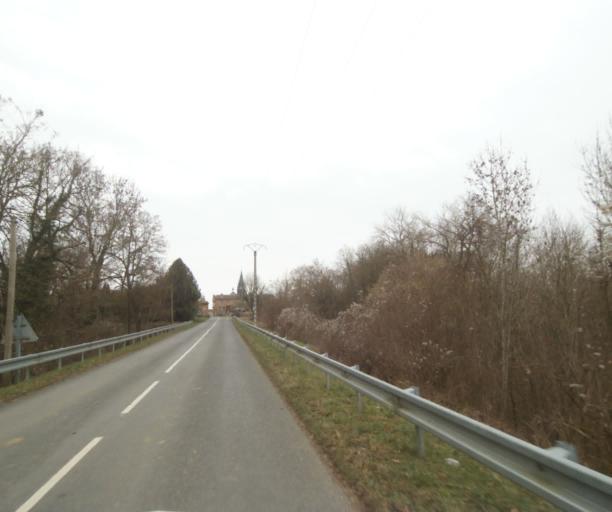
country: FR
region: Champagne-Ardenne
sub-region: Departement de la Haute-Marne
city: Villiers-en-Lieu
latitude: 48.6404
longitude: 4.7677
